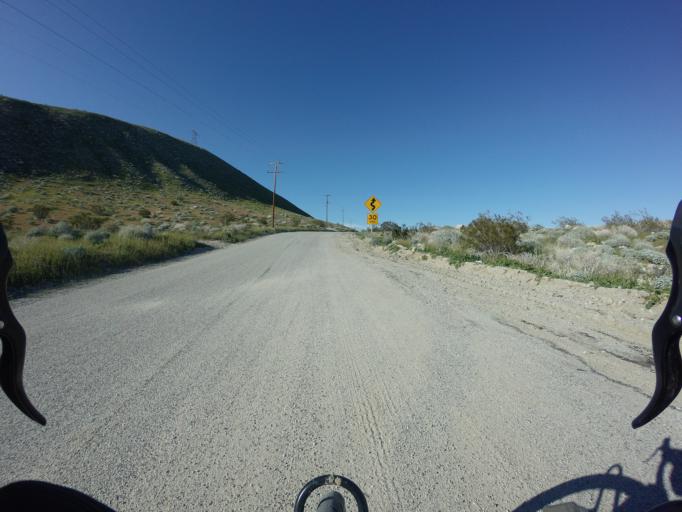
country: US
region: California
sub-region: Riverside County
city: Garnet
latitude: 33.9260
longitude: -116.6419
